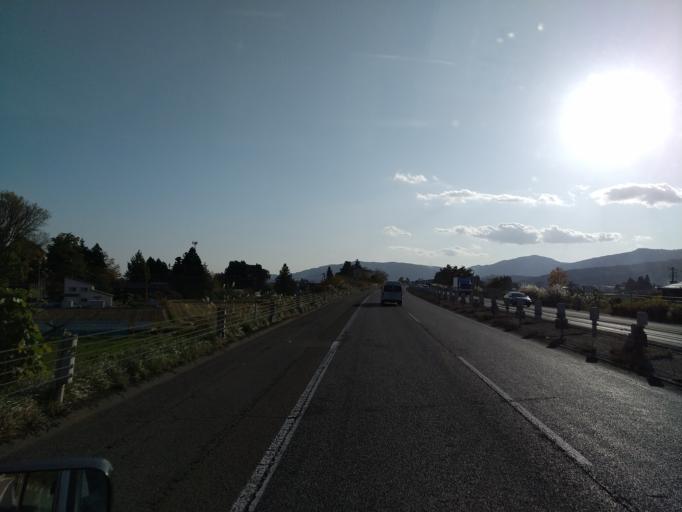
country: JP
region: Iwate
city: Morioka-shi
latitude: 39.6093
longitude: 141.1277
